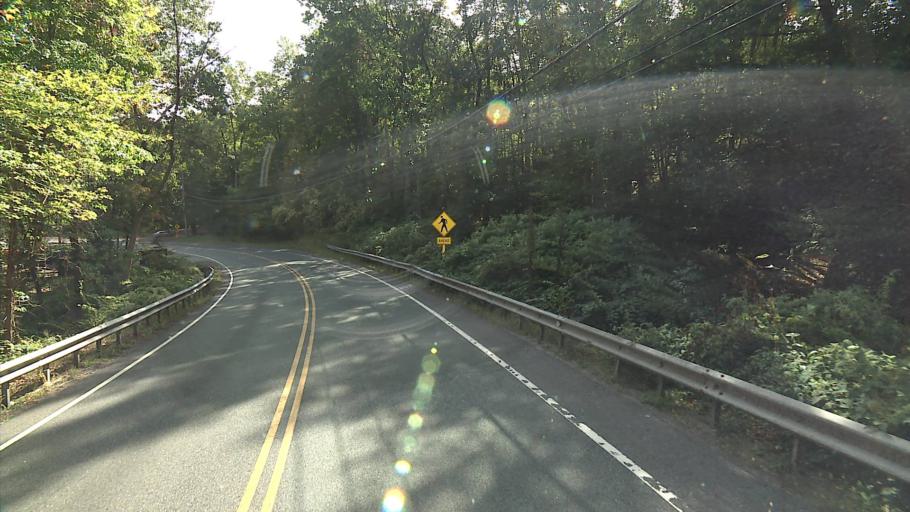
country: US
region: Connecticut
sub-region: New Haven County
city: Oxford
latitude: 41.3811
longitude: -73.1774
